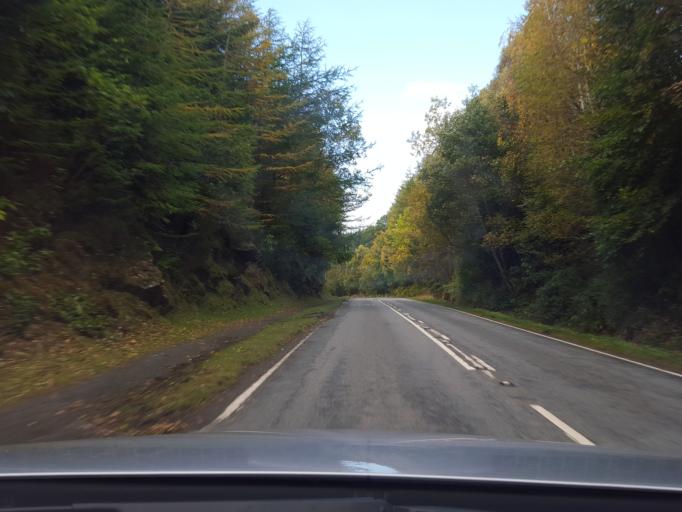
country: GB
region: Scotland
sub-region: Highland
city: Fort William
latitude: 57.2391
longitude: -5.4446
